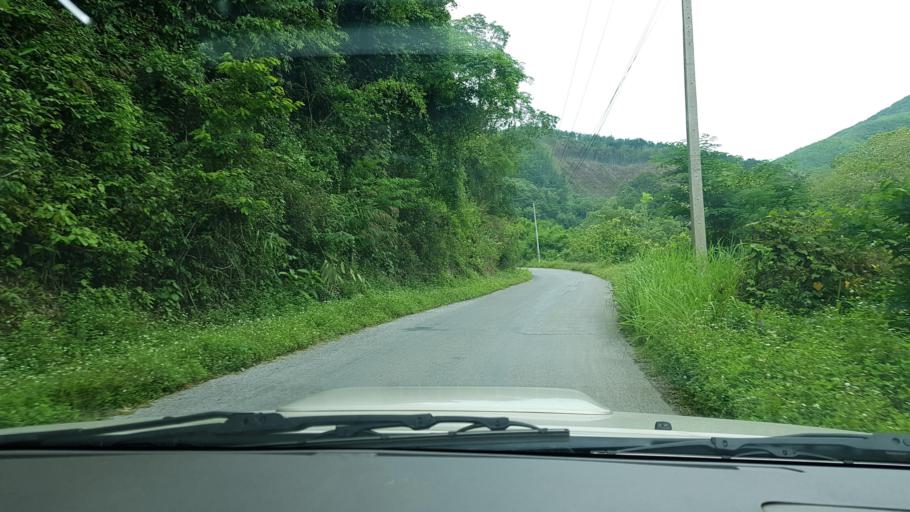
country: LA
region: Phongsali
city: Khoa
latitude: 21.0498
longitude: 102.4115
